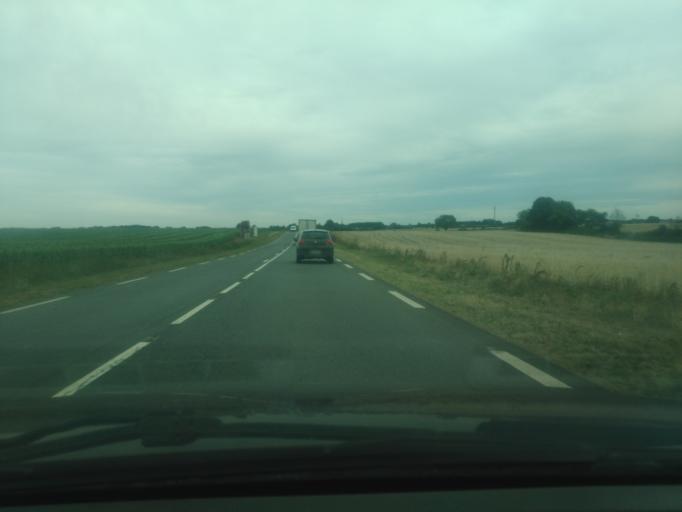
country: FR
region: Poitou-Charentes
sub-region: Departement de la Vienne
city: Saint-Savin
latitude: 46.5691
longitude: 0.8405
